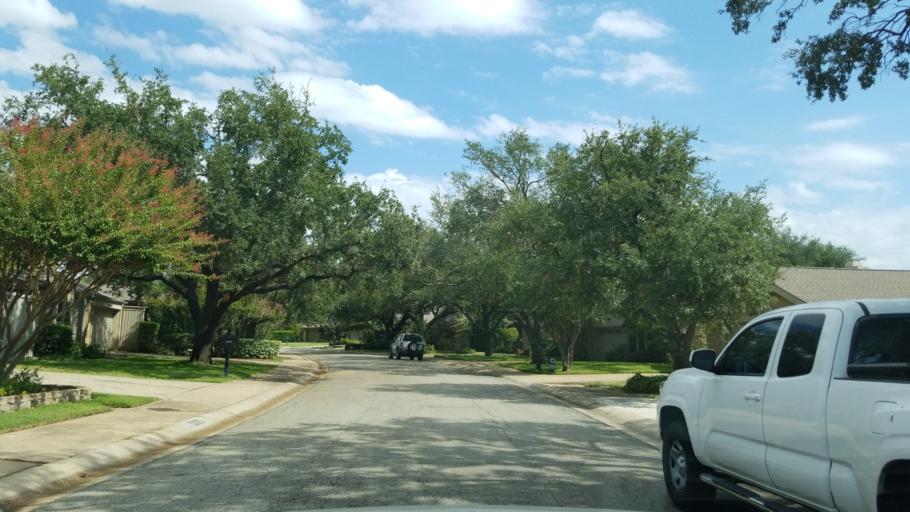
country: US
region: Texas
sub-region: Dallas County
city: Addison
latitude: 32.9611
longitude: -96.8028
